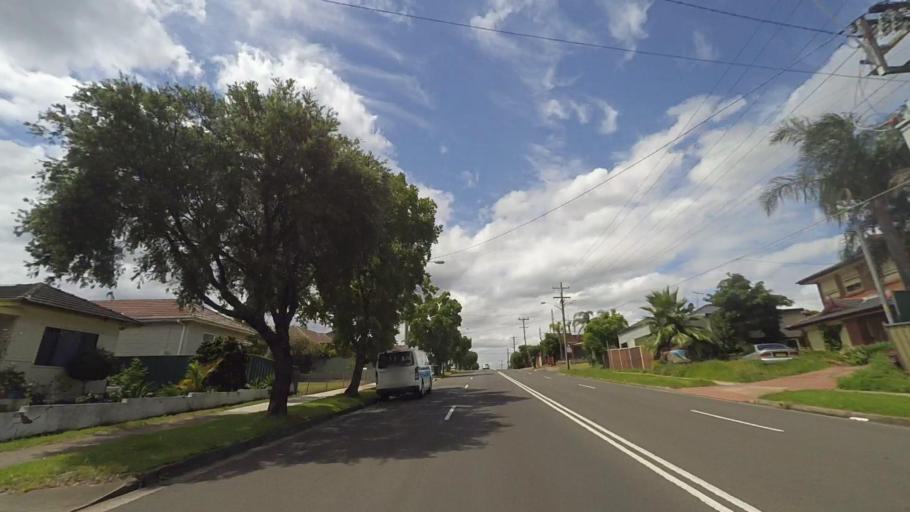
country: AU
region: New South Wales
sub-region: Fairfield
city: Fairfield Heights
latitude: -33.8764
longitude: 150.9433
